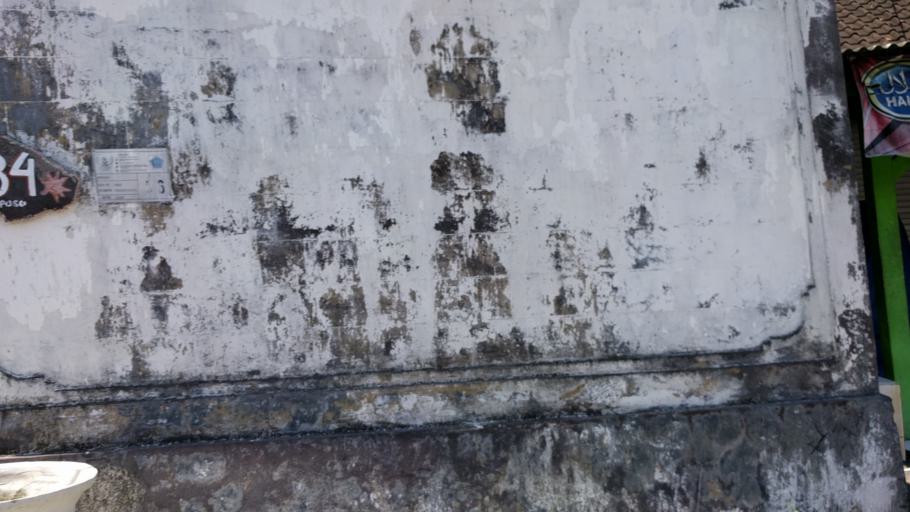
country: ID
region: Bali
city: Banjar Medura
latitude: -8.7053
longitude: 115.2575
